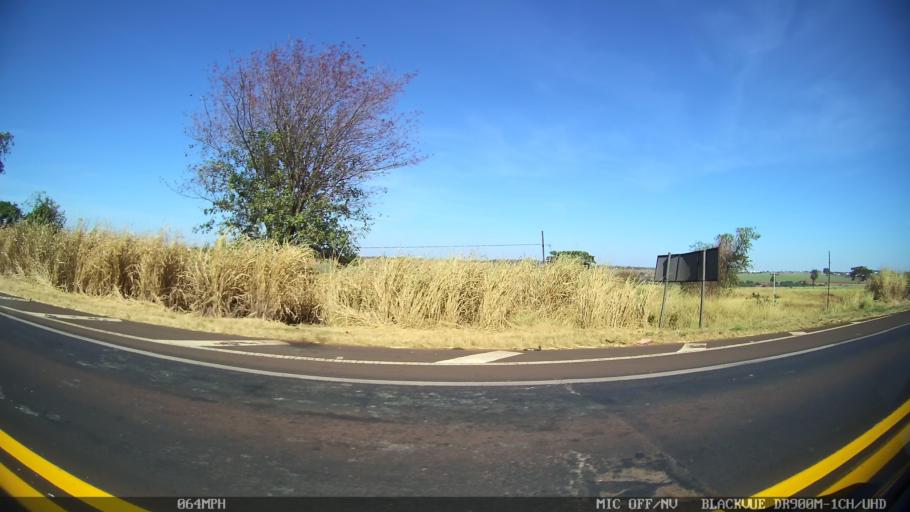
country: BR
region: Sao Paulo
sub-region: Barretos
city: Barretos
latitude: -20.5020
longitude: -48.5432
